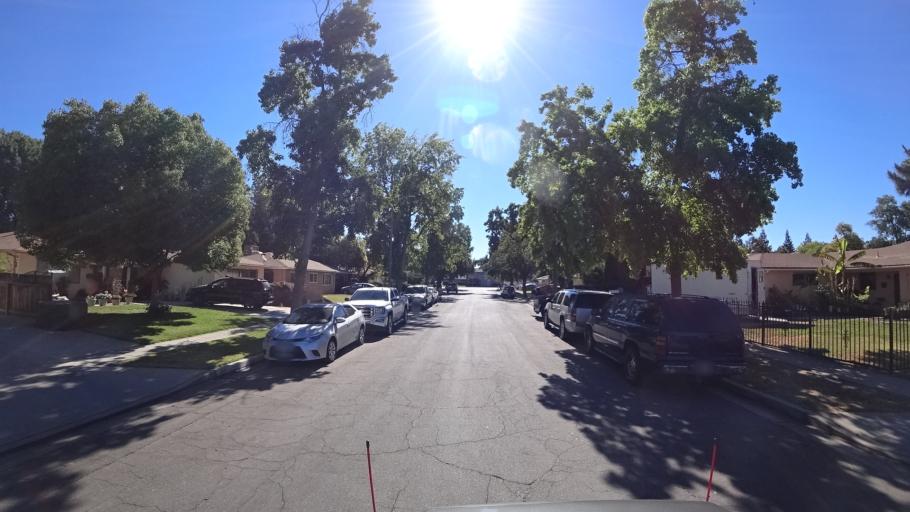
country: US
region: California
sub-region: Fresno County
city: Fresno
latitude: 36.8064
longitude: -119.8458
